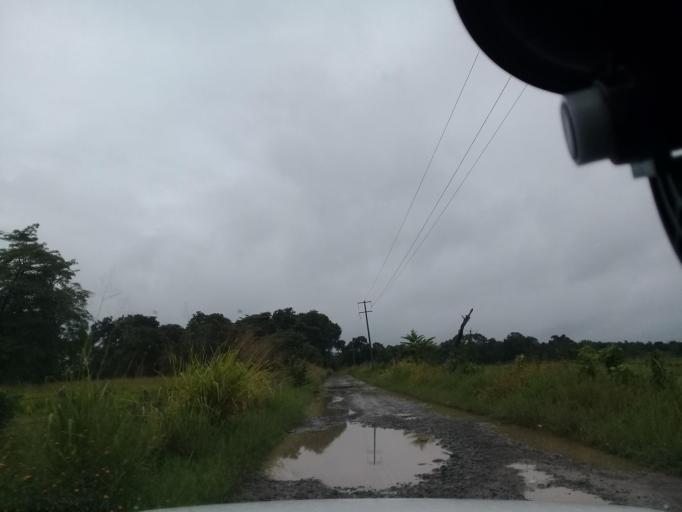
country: MX
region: Veracruz
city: Platon Sanchez
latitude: 21.2452
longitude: -98.3459
